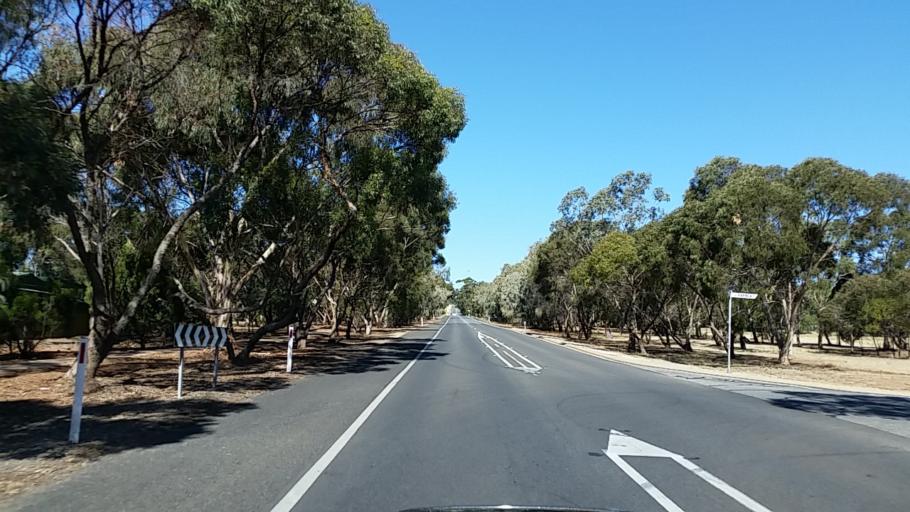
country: AU
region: South Australia
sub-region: Salisbury
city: Elizabeth
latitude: -34.7081
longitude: 138.7088
